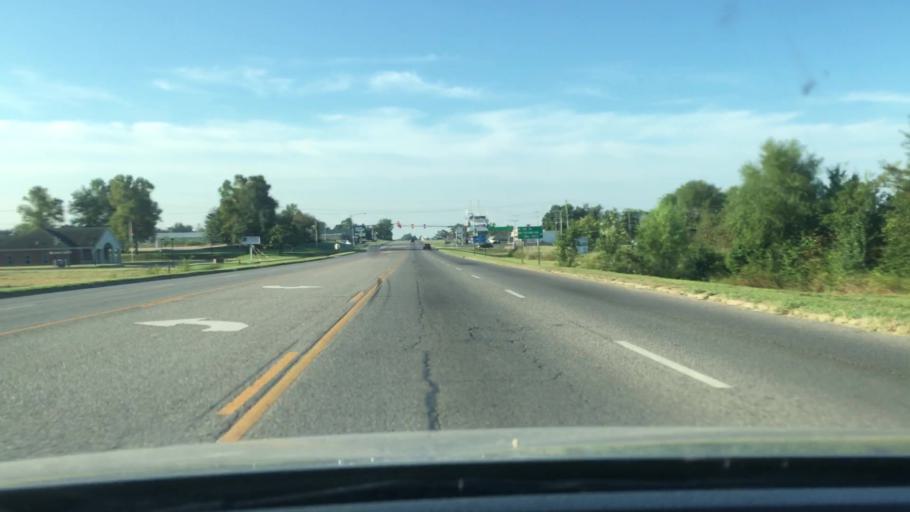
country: US
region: Oklahoma
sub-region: Cherokee County
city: Park Hill
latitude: 35.8731
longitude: -94.9763
